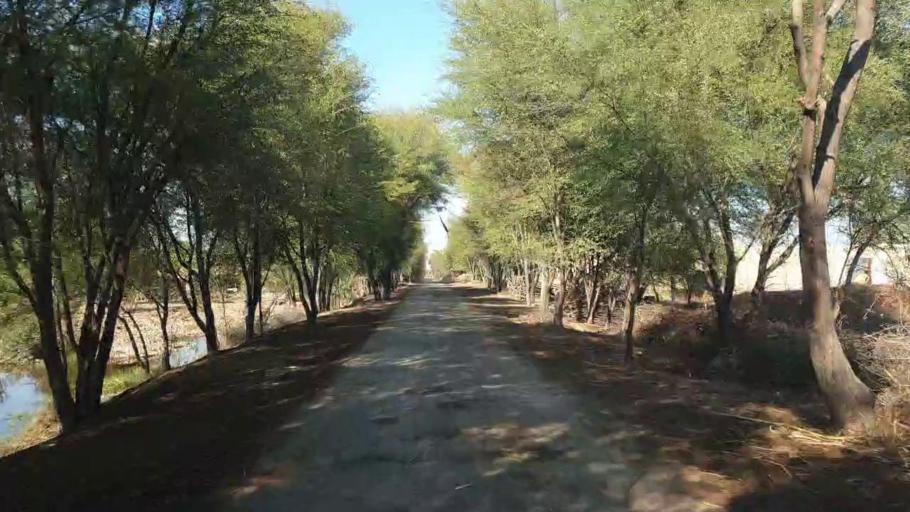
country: PK
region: Sindh
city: Shahdadpur
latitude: 25.9252
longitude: 68.5301
